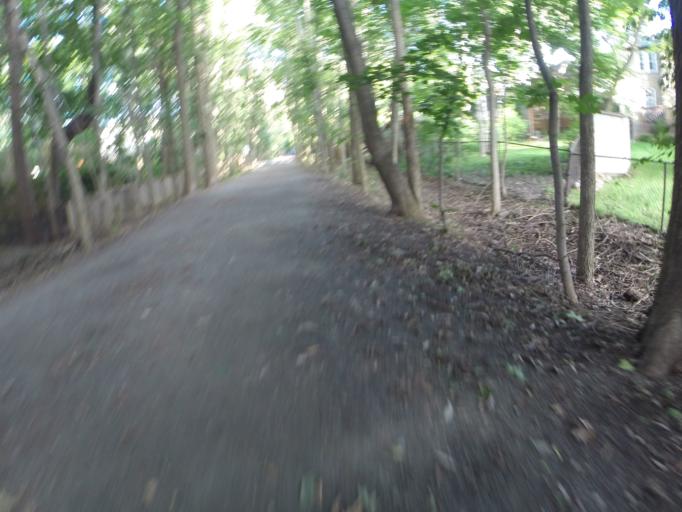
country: CA
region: Ontario
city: Toronto
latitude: 43.6992
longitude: -79.4088
